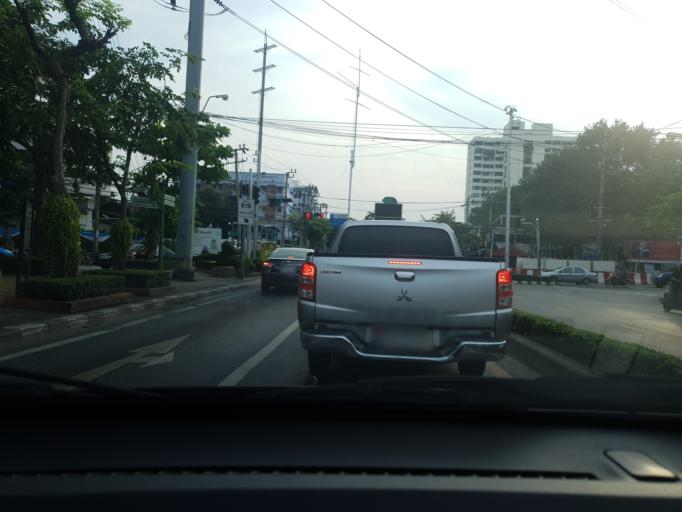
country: TH
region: Bangkok
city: Khlong San
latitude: 13.7300
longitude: 100.5082
